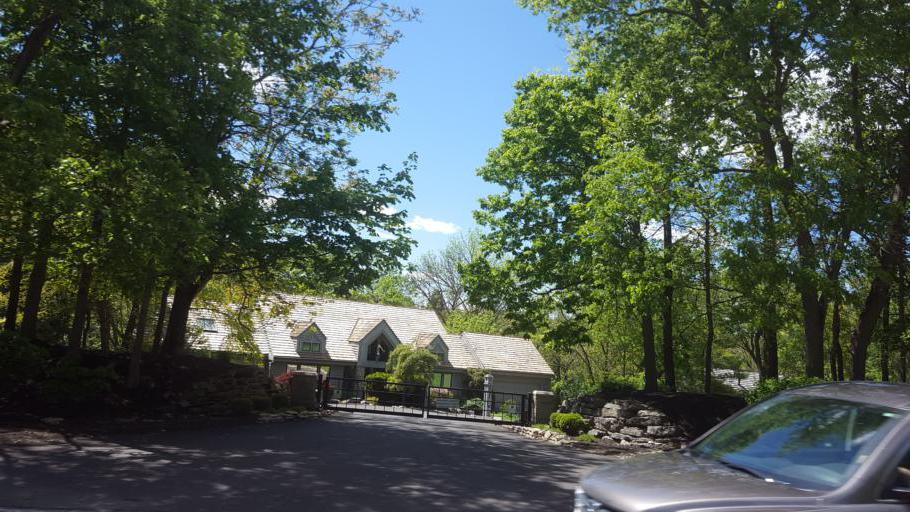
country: US
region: Ohio
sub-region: Franklin County
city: Dublin
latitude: 40.0839
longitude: -83.1103
